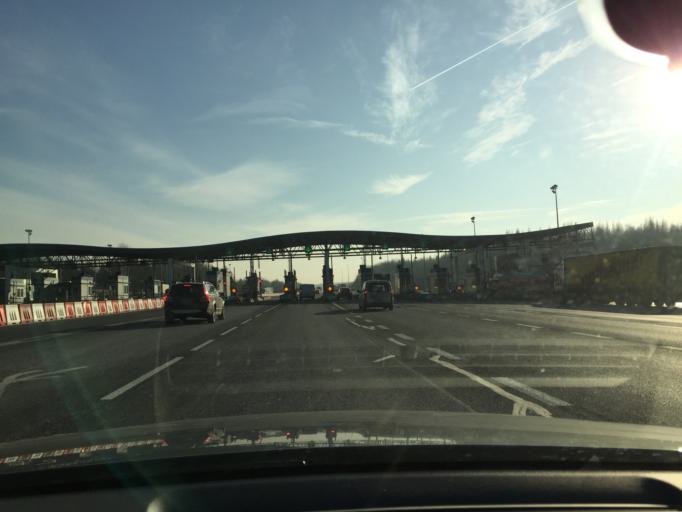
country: PL
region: Silesian Voivodeship
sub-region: Myslowice
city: Myslowice
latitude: 50.1974
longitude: 19.1852
